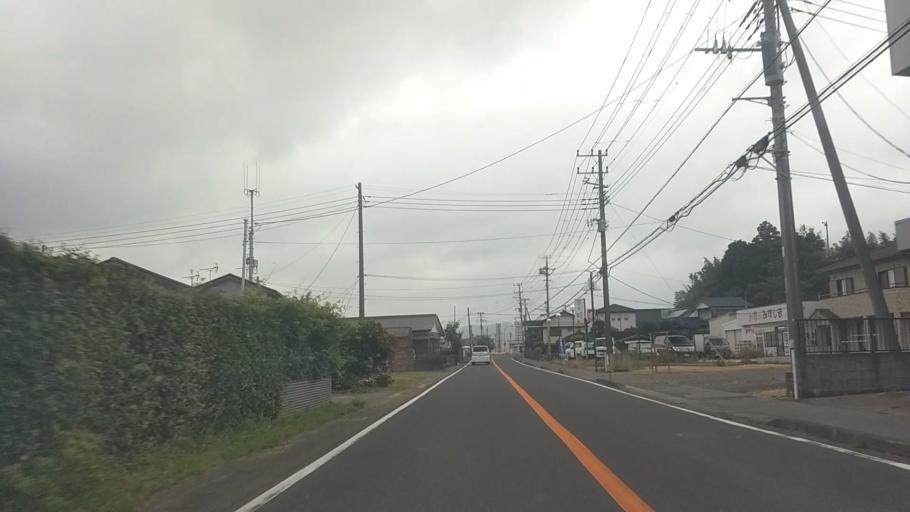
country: JP
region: Chiba
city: Kawaguchi
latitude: 35.1099
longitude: 140.0830
